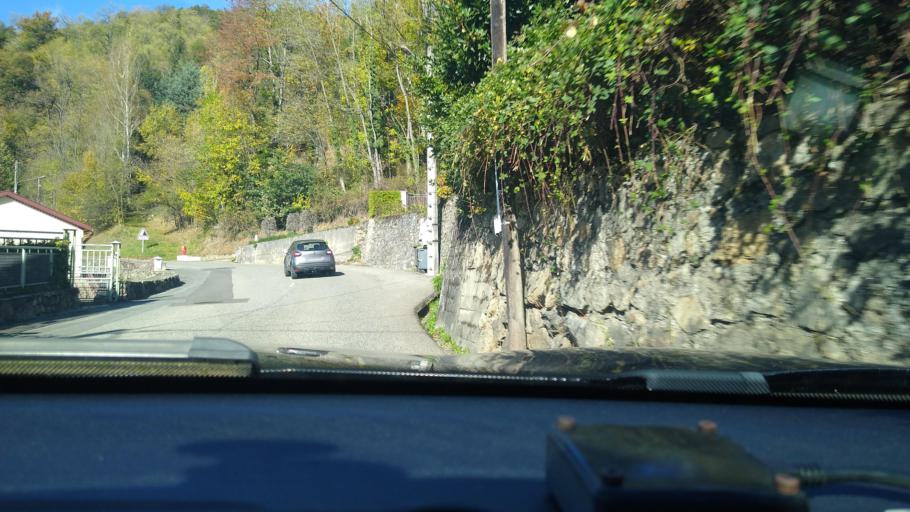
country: FR
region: Midi-Pyrenees
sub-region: Departement de l'Ariege
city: Ax-les-Thermes
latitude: 42.7207
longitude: 1.8432
